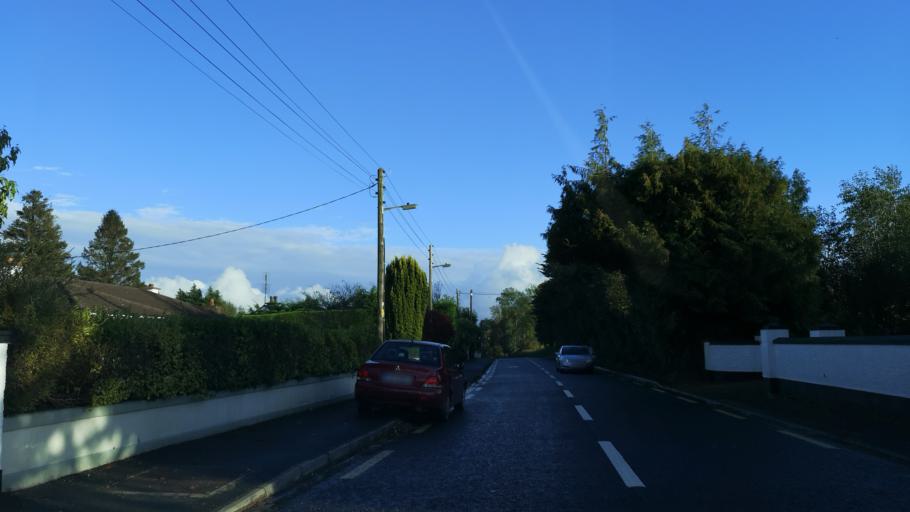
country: IE
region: Connaught
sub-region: Roscommon
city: Castlerea
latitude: 53.7631
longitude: -8.4764
